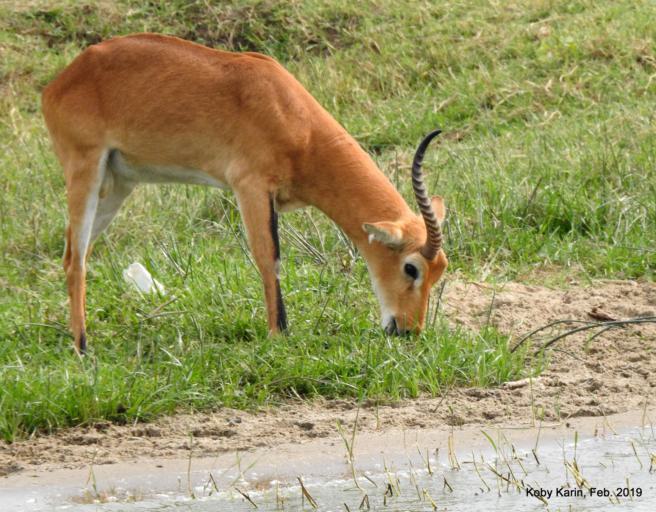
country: UG
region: Western Region
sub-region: Rubirizi District
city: Rubirizi
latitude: -0.2090
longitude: 29.8896
